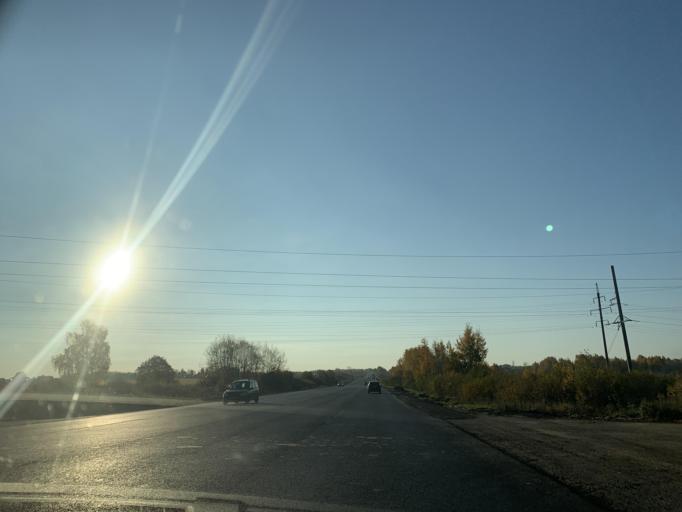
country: RU
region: Jaroslavl
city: Konstantinovskiy
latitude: 57.8006
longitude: 39.5948
